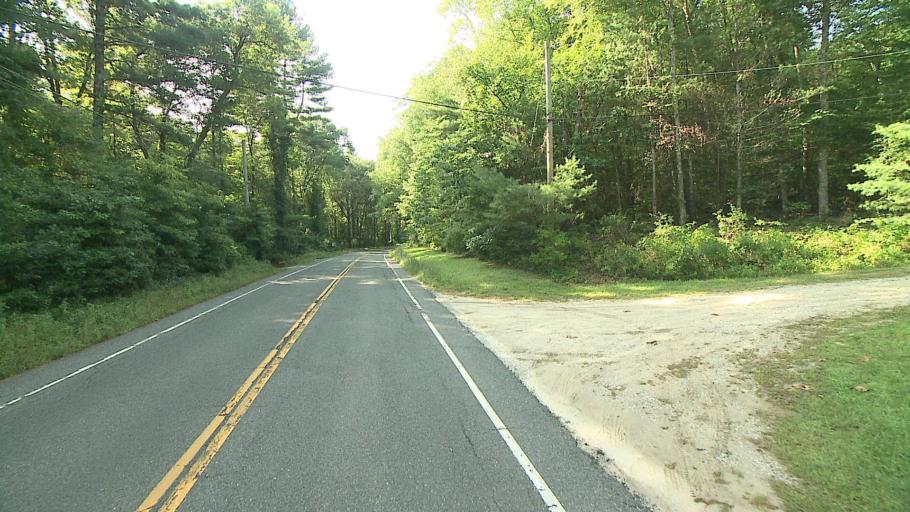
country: US
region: Connecticut
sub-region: Litchfield County
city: Canaan
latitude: 41.9140
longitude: -73.3649
